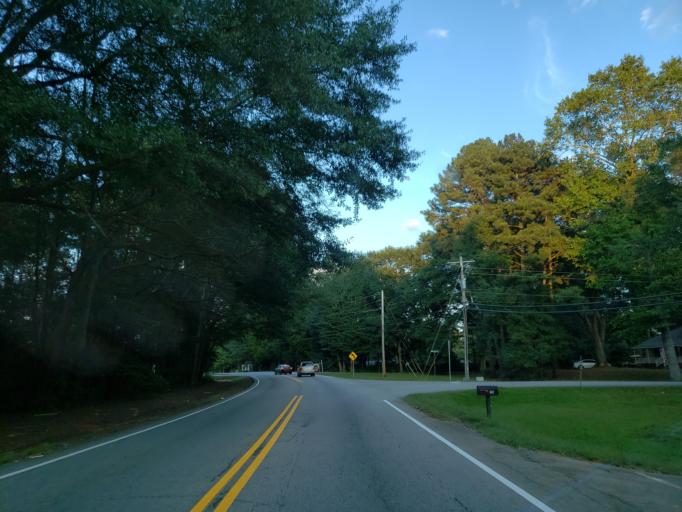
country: US
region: Georgia
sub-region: Carroll County
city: Carrollton
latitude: 33.6205
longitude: -85.0751
